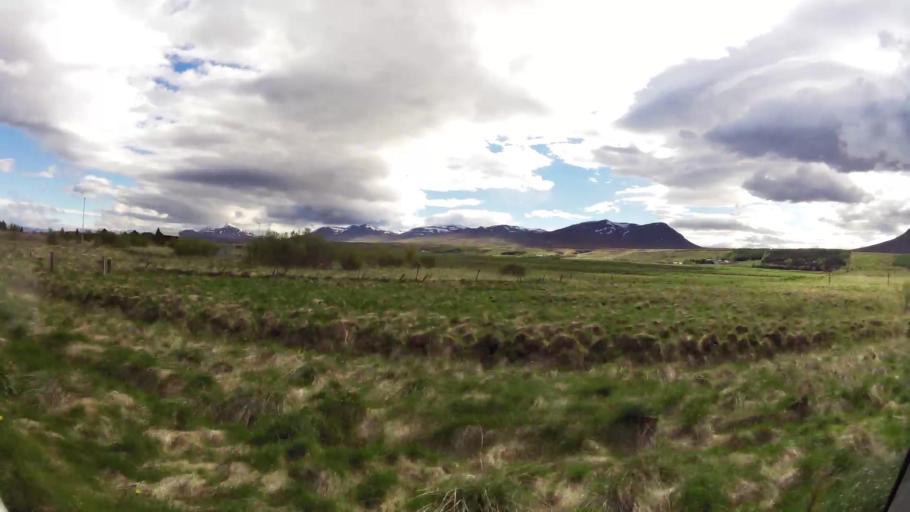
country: IS
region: Northwest
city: Saudarkrokur
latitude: 65.5506
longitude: -19.4565
